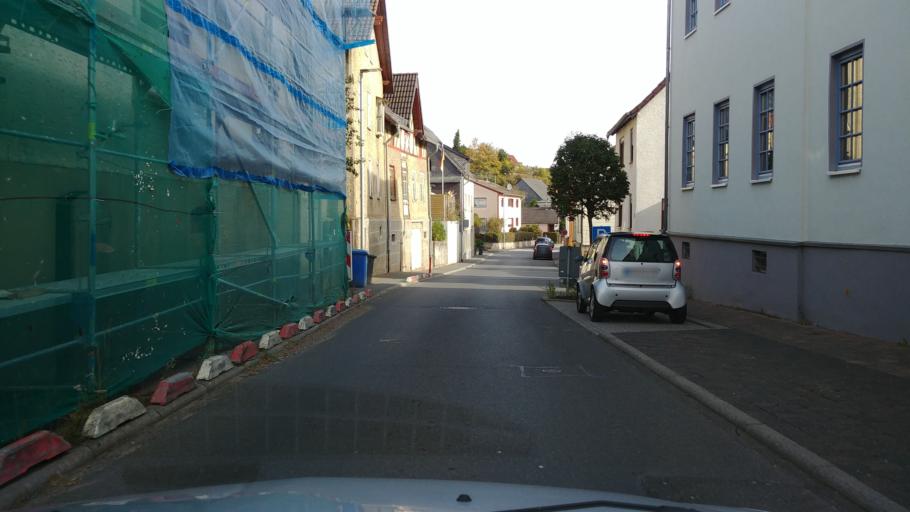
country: DE
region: Rheinland-Pfalz
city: Reckenroth
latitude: 50.2134
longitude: 7.9968
